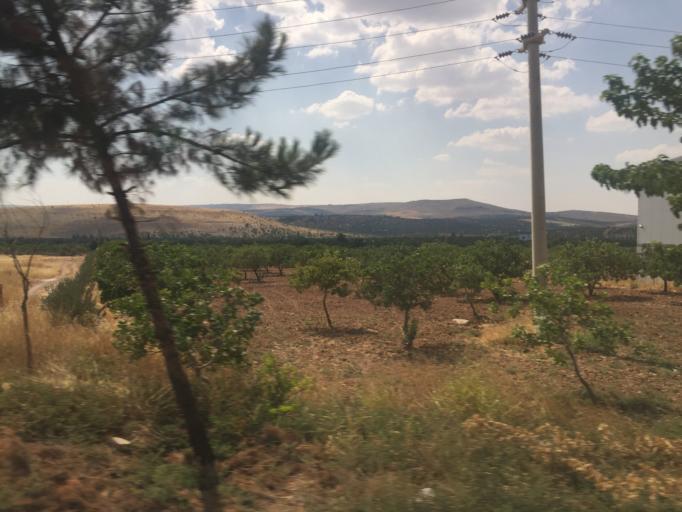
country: TR
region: Sanliurfa
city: Sanliurfa
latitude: 37.2461
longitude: 38.7934
